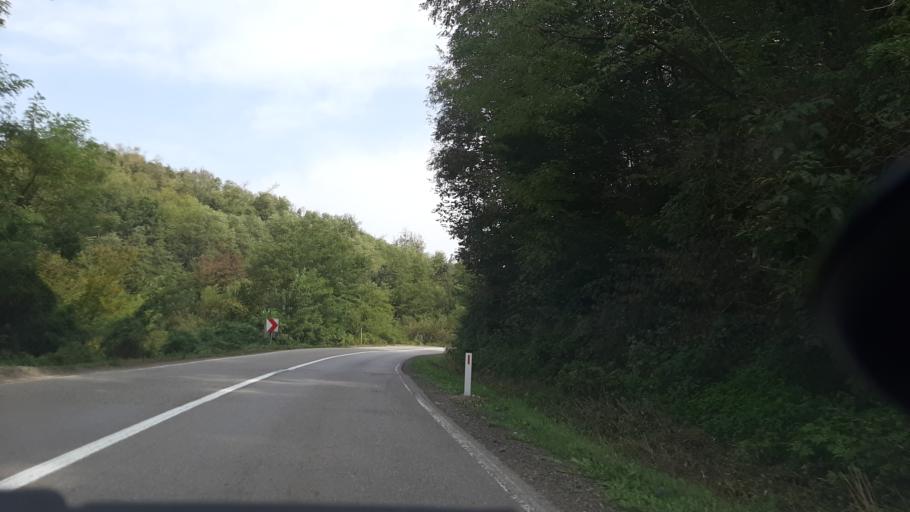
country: BA
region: Republika Srpska
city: Laktasi
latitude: 44.8773
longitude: 17.3629
